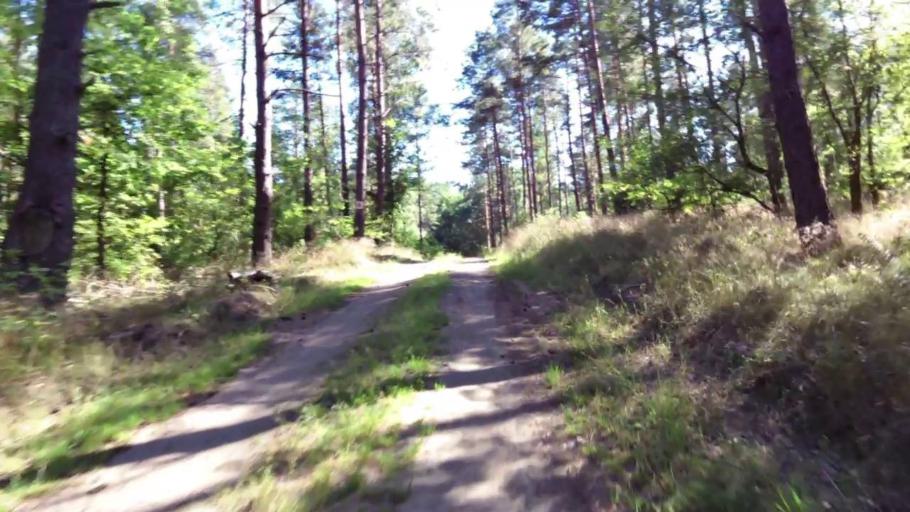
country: PL
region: West Pomeranian Voivodeship
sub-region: Powiat szczecinecki
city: Borne Sulinowo
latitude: 53.6017
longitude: 16.6072
